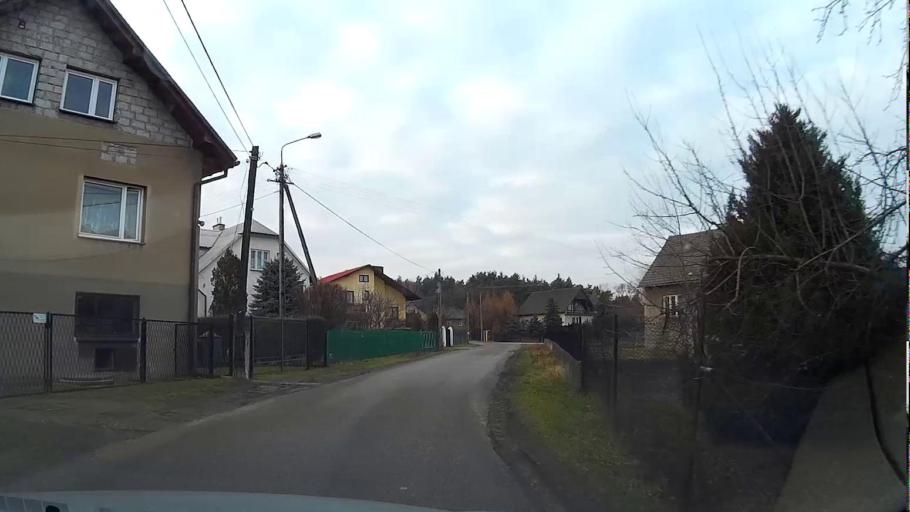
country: PL
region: Lesser Poland Voivodeship
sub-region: Powiat chrzanowski
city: Kwaczala
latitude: 50.0631
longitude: 19.4800
